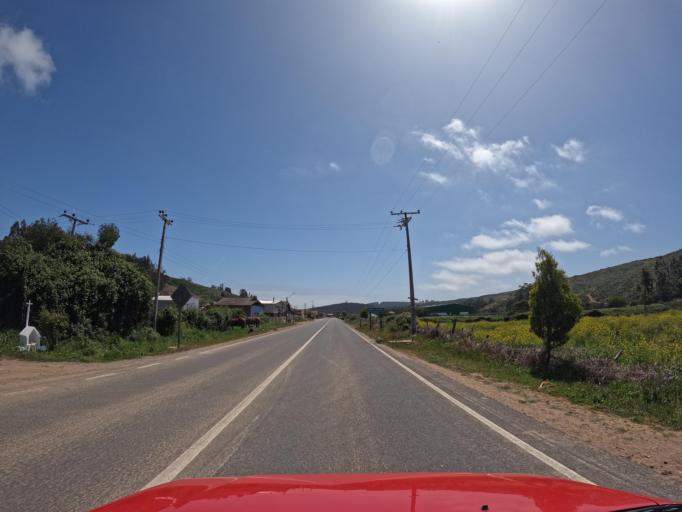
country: CL
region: O'Higgins
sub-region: Provincia de Colchagua
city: Santa Cruz
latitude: -34.6480
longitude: -72.0304
